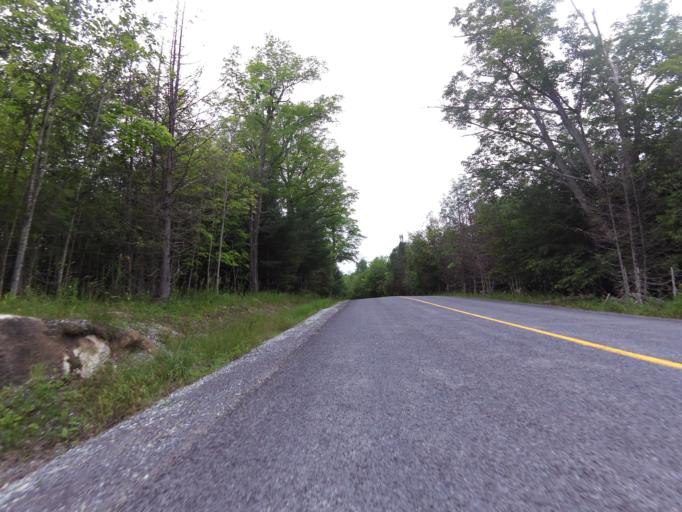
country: CA
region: Ontario
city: Perth
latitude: 44.8839
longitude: -76.5216
